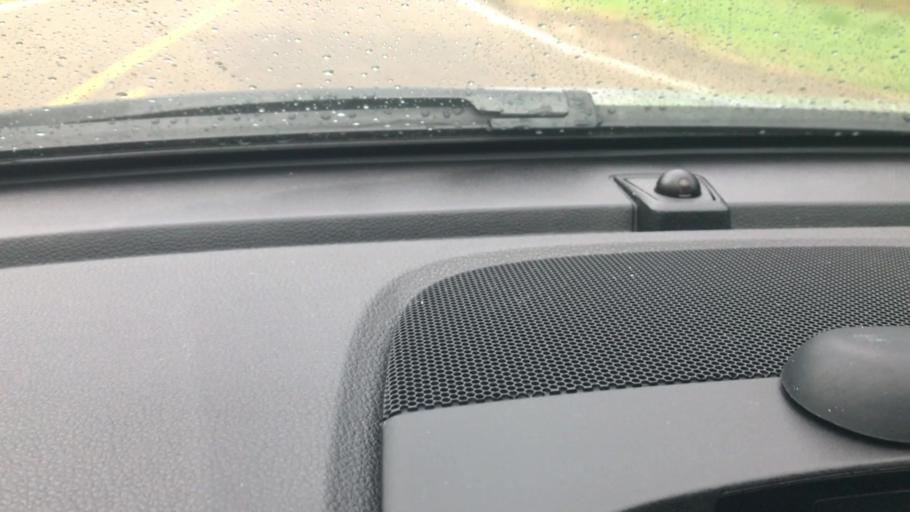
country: US
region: Mississippi
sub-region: Pike County
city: Summit
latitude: 31.3577
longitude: -90.6182
